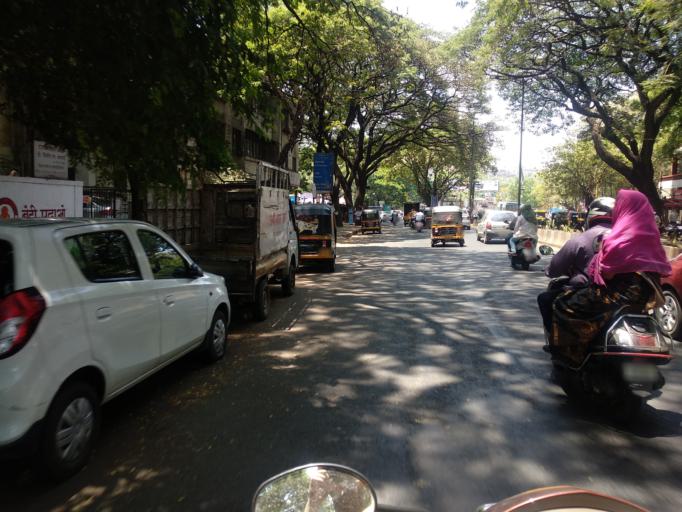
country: IN
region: Maharashtra
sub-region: Pune Division
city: Pune
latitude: 18.5039
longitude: 73.8454
